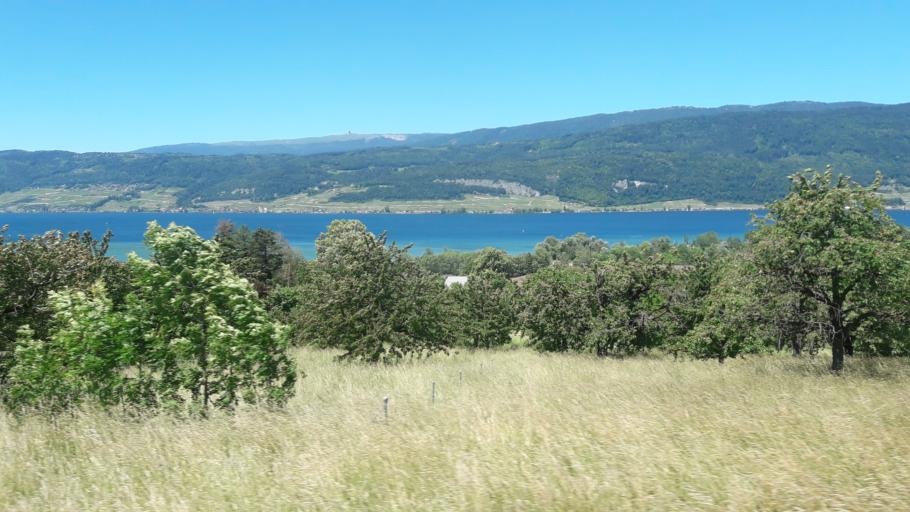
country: CH
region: Bern
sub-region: Seeland District
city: Tauffelen
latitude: 47.0832
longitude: 7.2100
